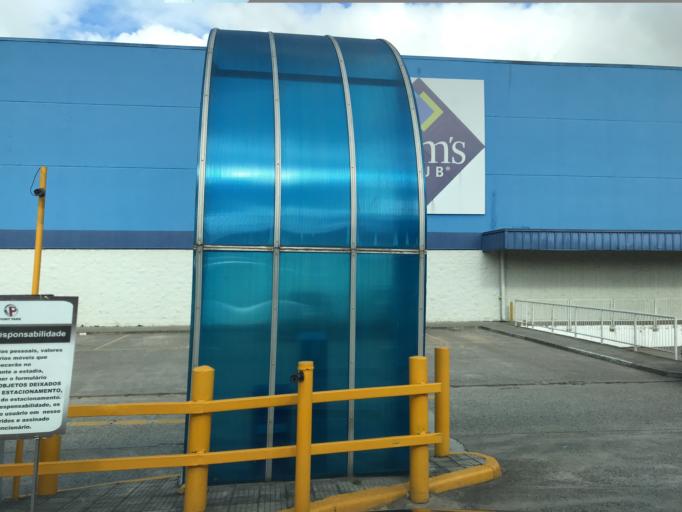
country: BR
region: Sao Paulo
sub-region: Carapicuiba
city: Carapicuiba
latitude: -23.5008
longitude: -46.8371
